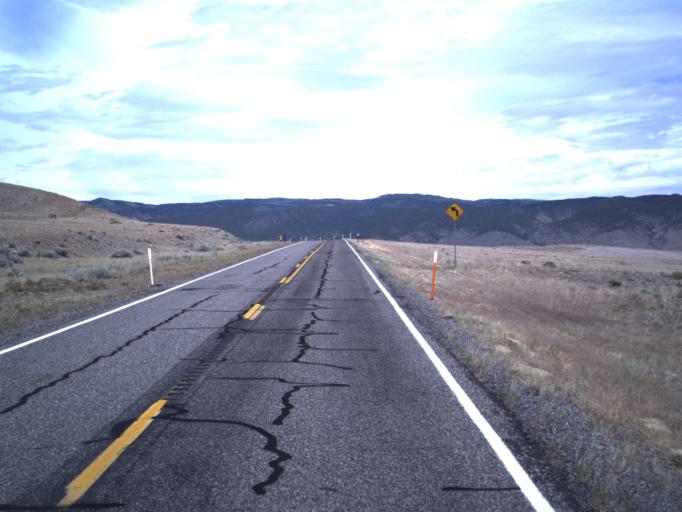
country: US
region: Utah
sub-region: Sevier County
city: Monroe
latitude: 38.6317
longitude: -112.1725
